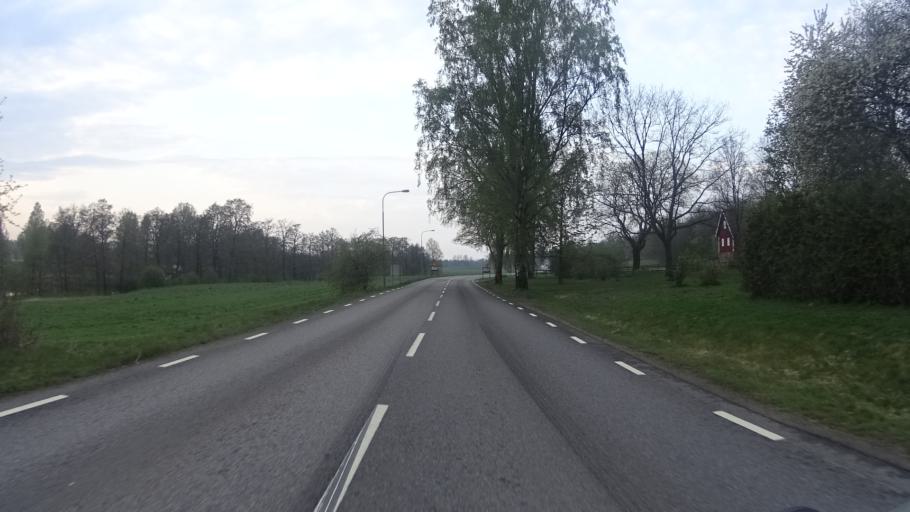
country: SE
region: Kronoberg
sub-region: Ljungby Kommun
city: Ljungby
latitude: 56.8428
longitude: 13.9712
